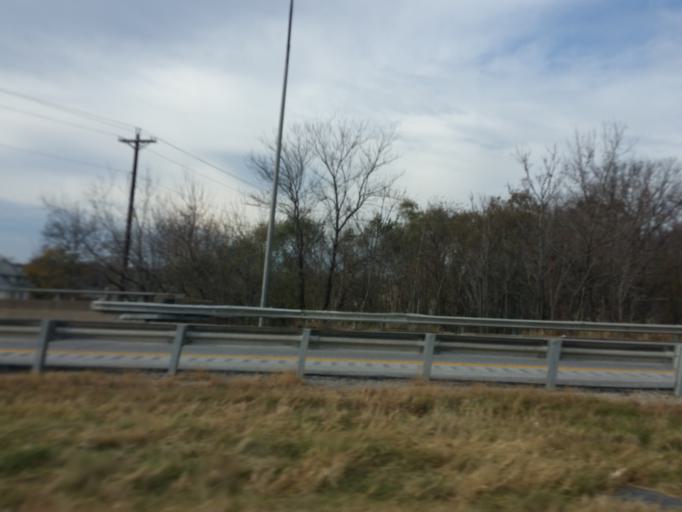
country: US
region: Illinois
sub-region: Rock Island County
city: Moline
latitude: 41.4753
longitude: -90.4941
